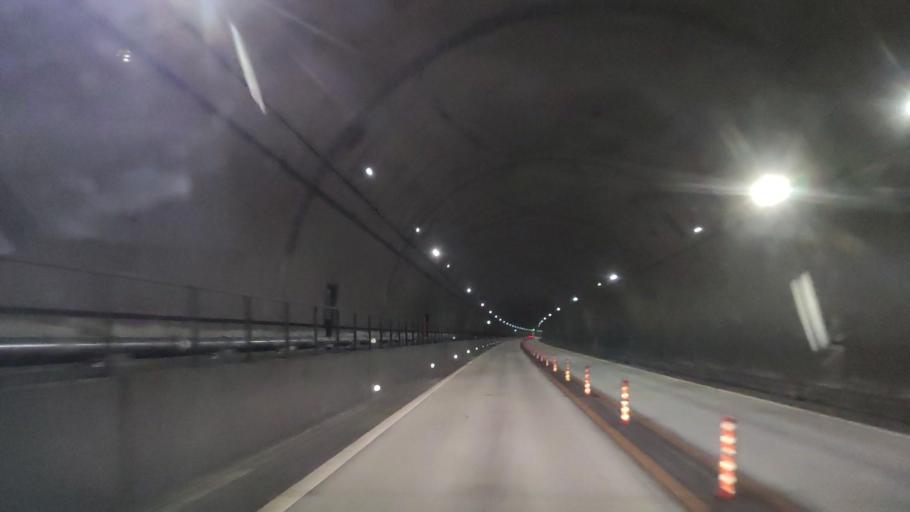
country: JP
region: Ehime
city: Hojo
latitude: 34.0794
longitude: 132.9763
